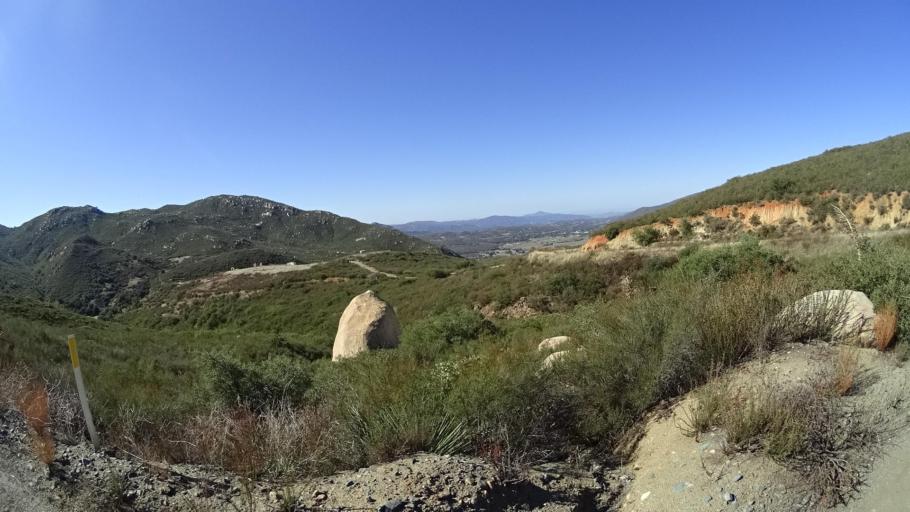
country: US
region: California
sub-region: San Diego County
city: Descanso
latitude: 32.8681
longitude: -116.6544
